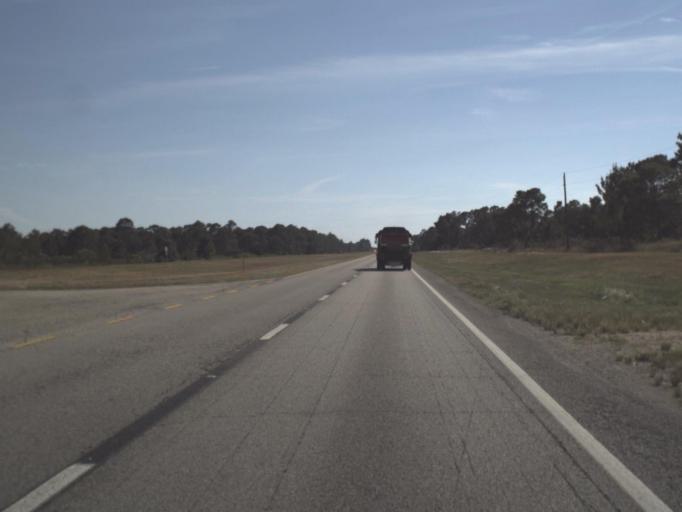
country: US
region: Florida
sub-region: Highlands County
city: Placid Lakes
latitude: 27.1077
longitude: -81.3323
